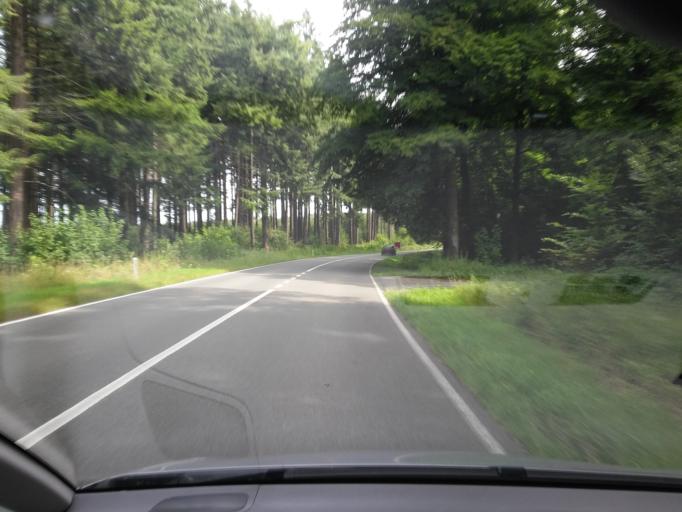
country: BE
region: Wallonia
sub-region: Province du Luxembourg
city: Chiny
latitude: 49.7753
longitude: 5.3272
